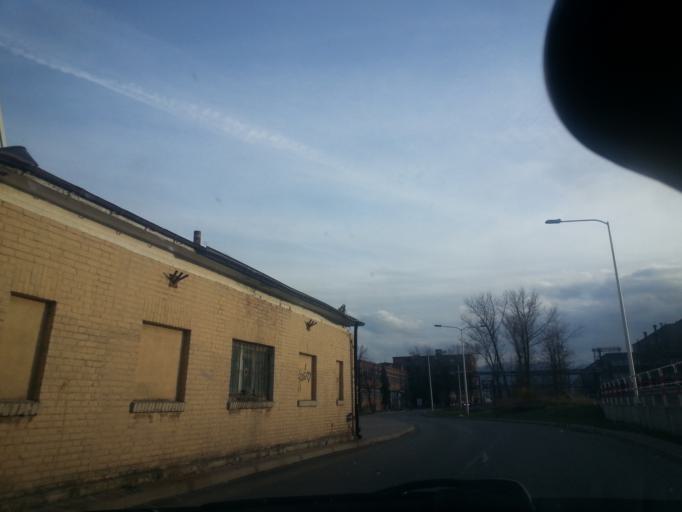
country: PL
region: Lower Silesian Voivodeship
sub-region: Jelenia Gora
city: Jelenia Gora
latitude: 50.8910
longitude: 15.7113
